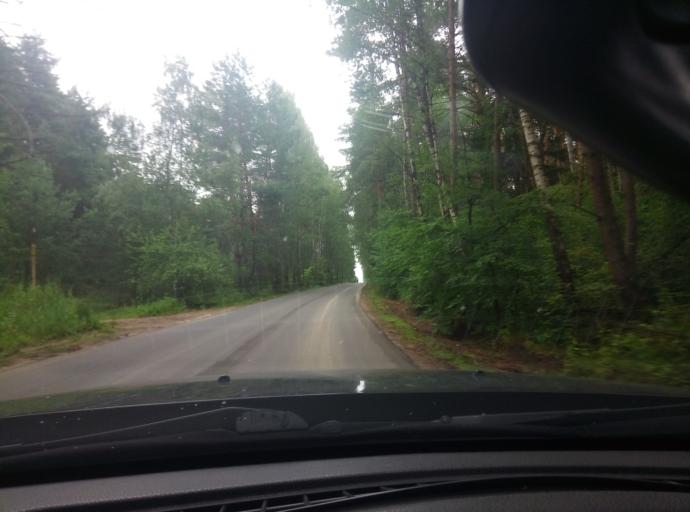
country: RU
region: Kaluga
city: Zhukovo
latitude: 54.9554
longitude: 36.7758
